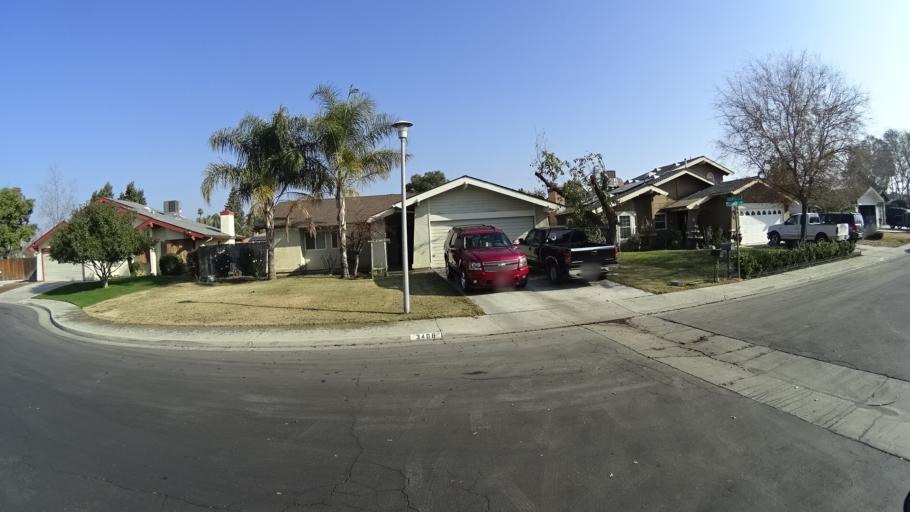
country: US
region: California
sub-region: Kern County
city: Greenacres
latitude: 35.3228
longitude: -119.0916
